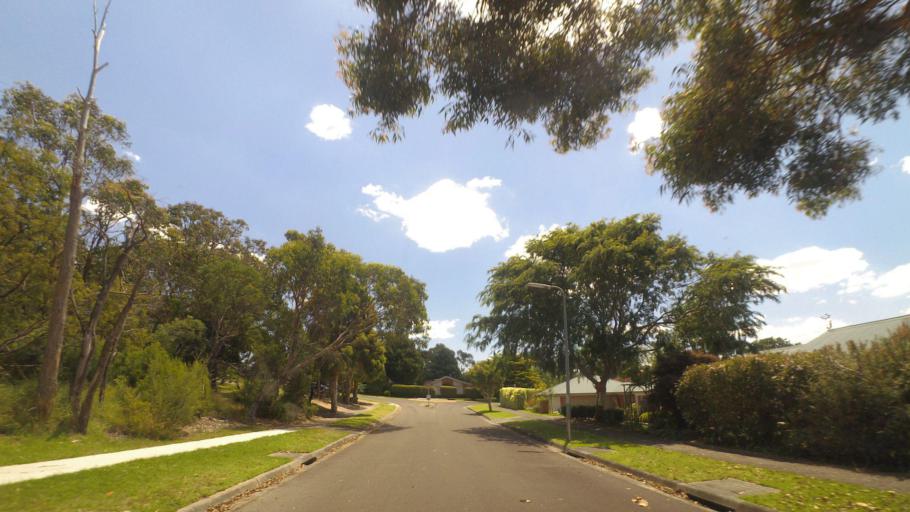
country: AU
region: Victoria
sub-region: Yarra Ranges
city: Kilsyth
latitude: -37.8031
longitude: 145.3343
